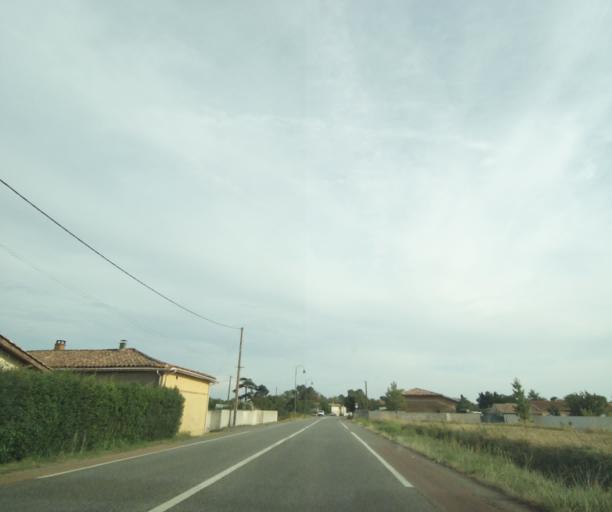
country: FR
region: Midi-Pyrenees
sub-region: Departement du Tarn-et-Garonne
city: Verdun-sur-Garonne
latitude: 43.8662
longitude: 1.2672
